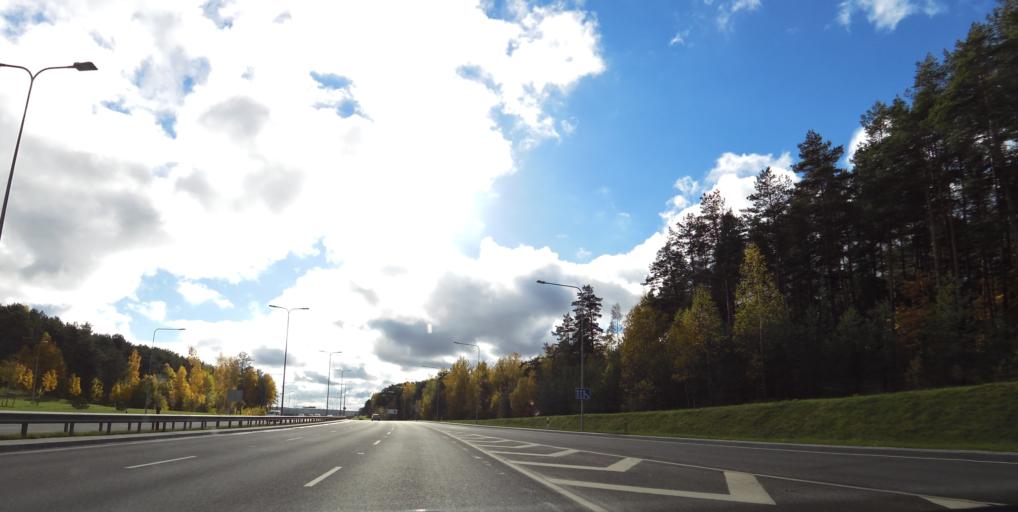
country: LT
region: Vilnius County
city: Lazdynai
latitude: 54.6819
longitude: 25.1942
